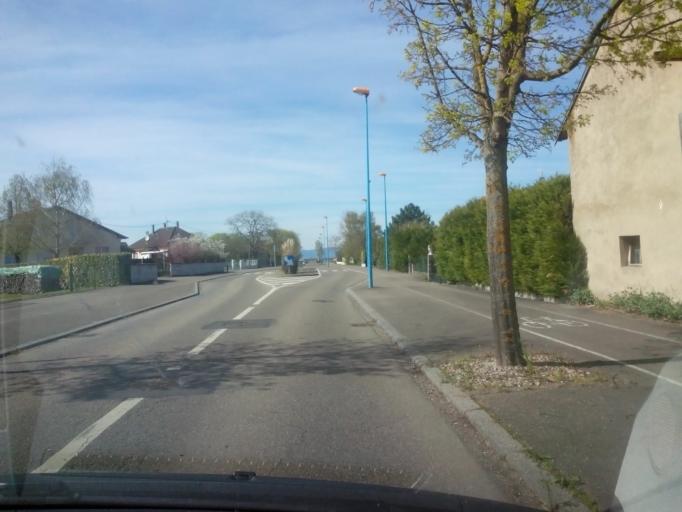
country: FR
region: Alsace
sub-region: Departement du Haut-Rhin
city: Algolsheim
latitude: 47.9735
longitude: 7.5371
